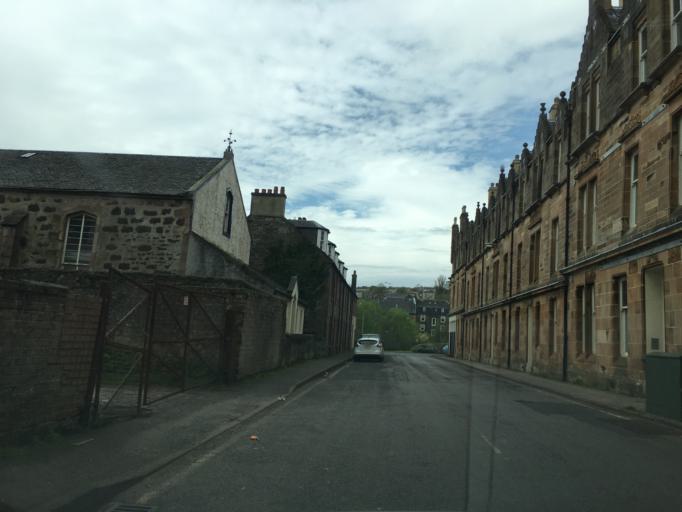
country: GB
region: Scotland
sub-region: Argyll and Bute
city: Rothesay
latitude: 55.8349
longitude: -5.0552
